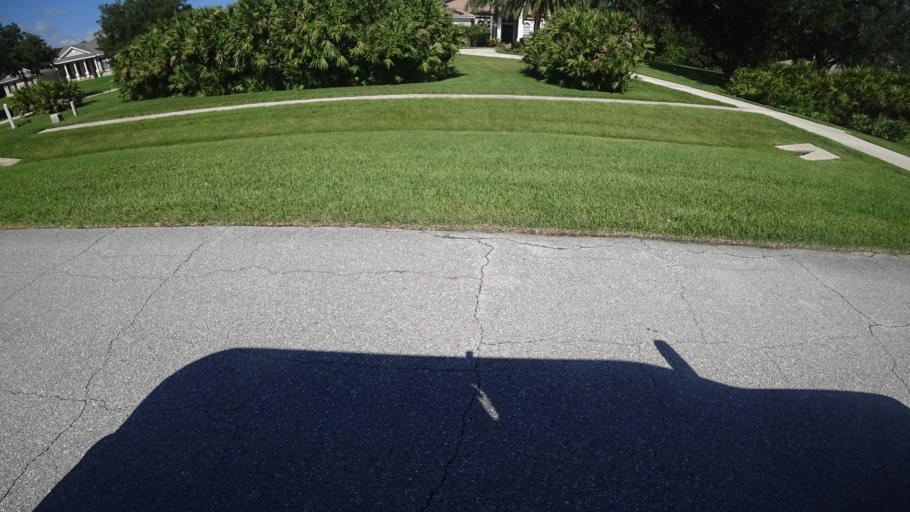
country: US
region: Florida
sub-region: Sarasota County
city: Fruitville
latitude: 27.3958
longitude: -82.3195
